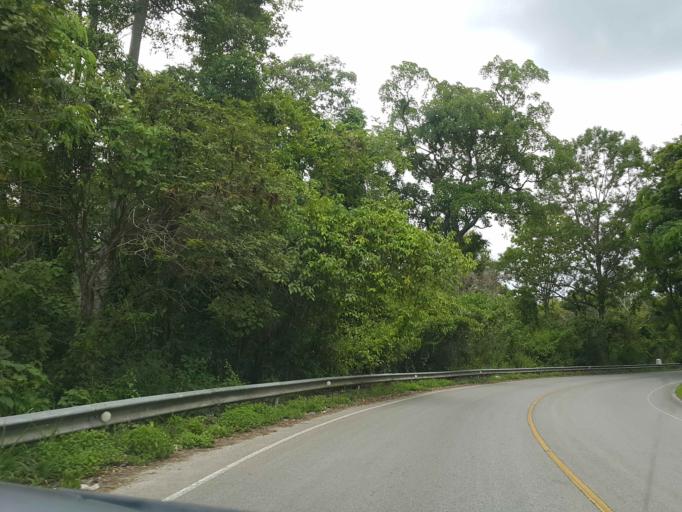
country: TH
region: Chiang Mai
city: Hang Dong
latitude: 18.7796
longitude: 98.8523
